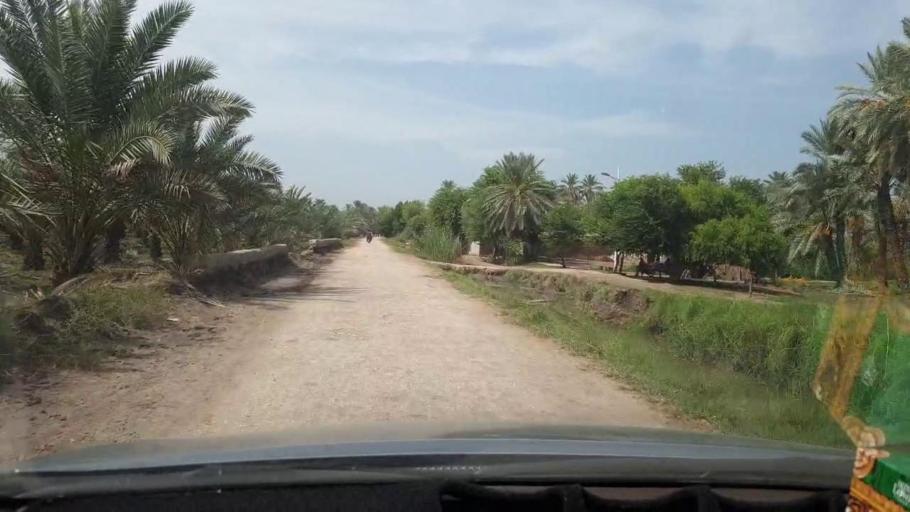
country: PK
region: Sindh
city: Khairpur
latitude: 27.4903
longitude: 68.7543
